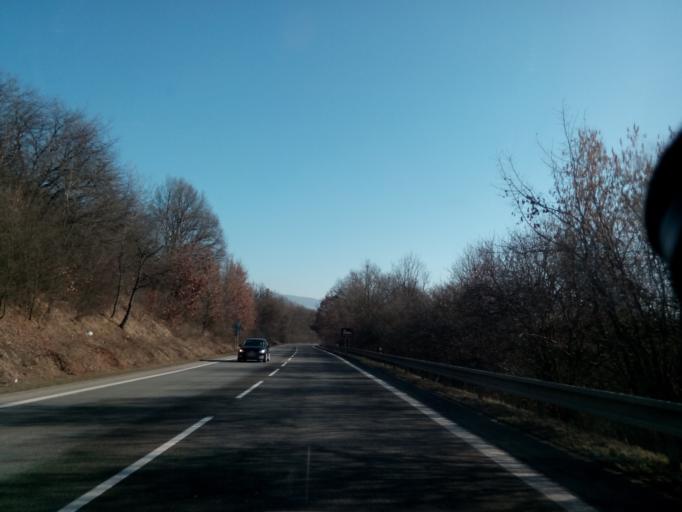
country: SK
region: Kosicky
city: Kosice
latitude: 48.7302
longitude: 21.4500
